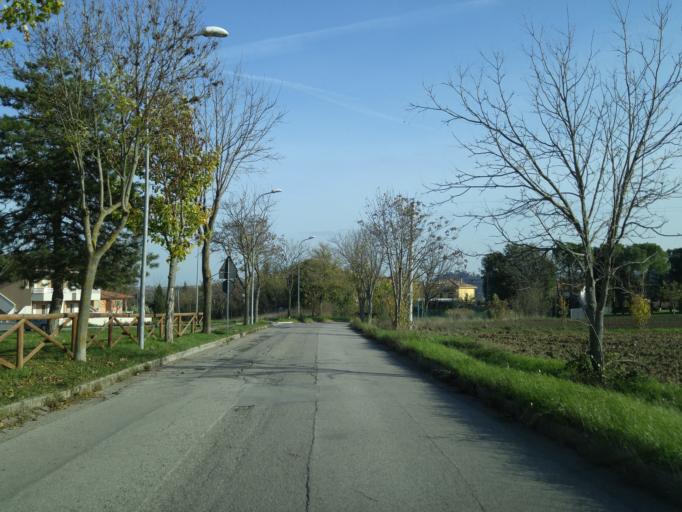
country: IT
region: The Marches
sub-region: Provincia di Pesaro e Urbino
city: Calcinelli
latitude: 43.7510
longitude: 12.9108
